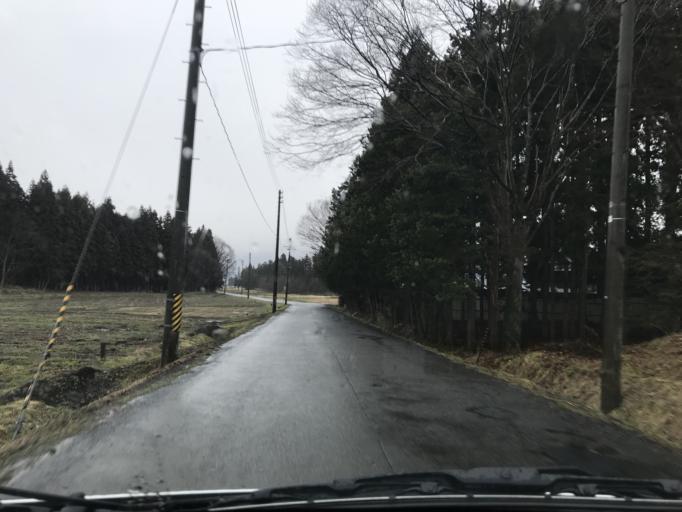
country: JP
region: Iwate
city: Kitakami
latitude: 39.2194
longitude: 141.0570
